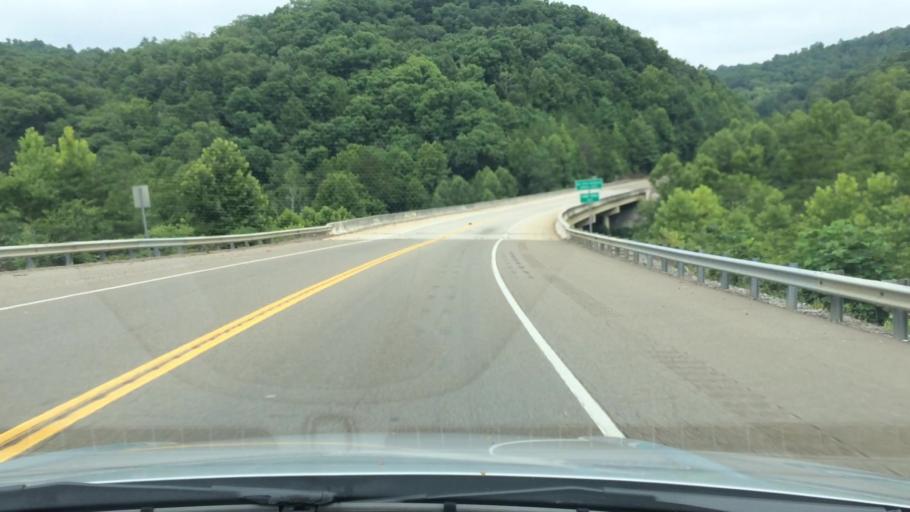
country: US
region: Tennessee
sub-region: Scott County
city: Huntsville
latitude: 36.4032
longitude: -84.4495
